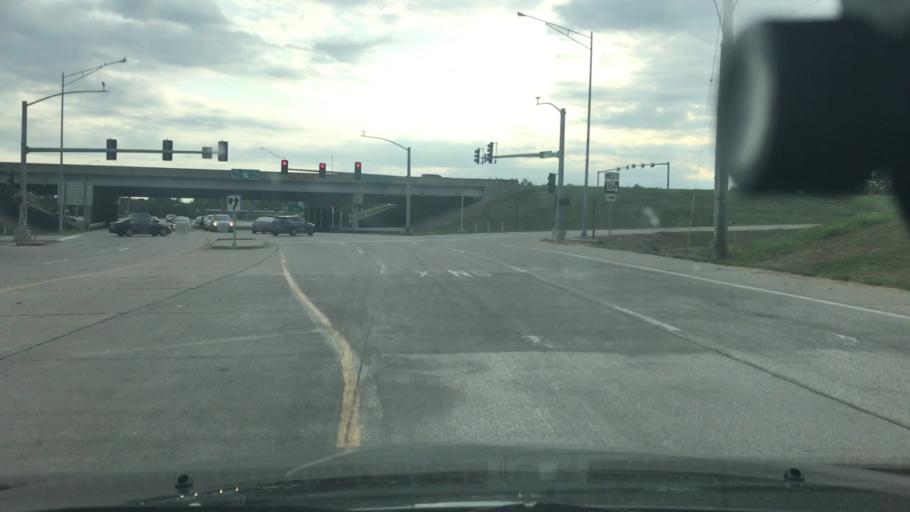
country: US
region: Missouri
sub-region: Saint Charles County
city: Saint Charles
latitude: 38.7447
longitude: -90.5286
